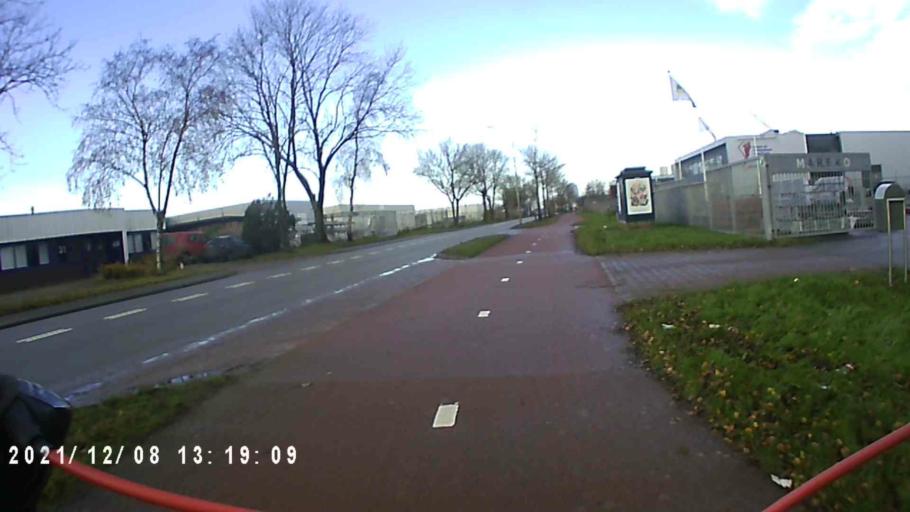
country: NL
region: Groningen
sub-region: Gemeente Haren
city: Haren
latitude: 53.1990
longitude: 6.6075
